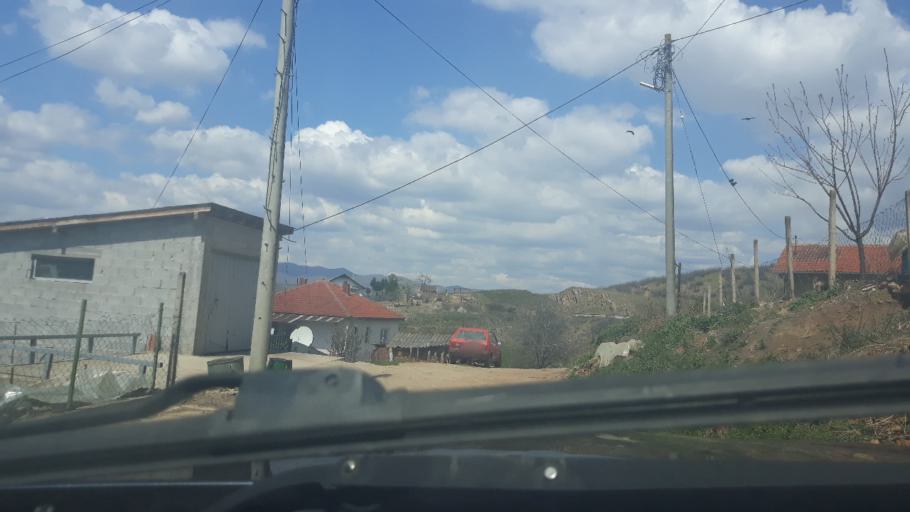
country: MK
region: Caska
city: Caska
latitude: 41.6518
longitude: 21.6936
